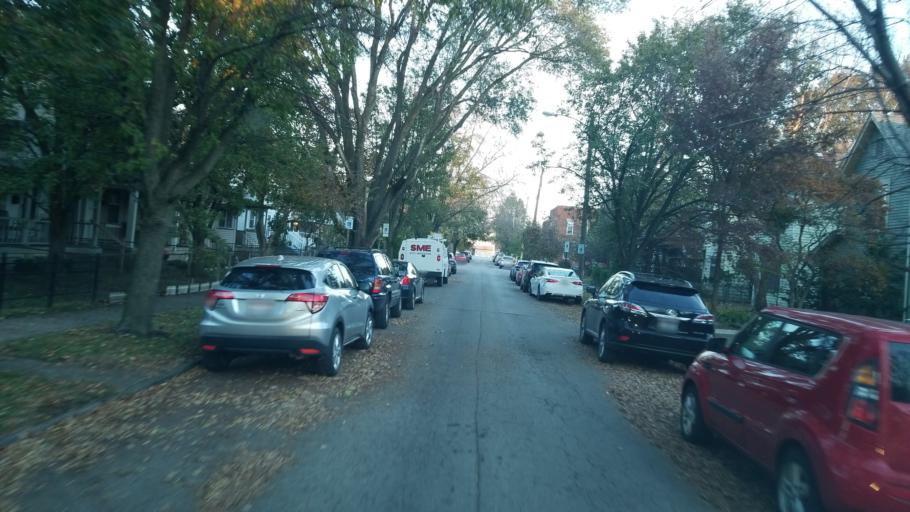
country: US
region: Ohio
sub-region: Franklin County
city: Columbus
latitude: 39.9383
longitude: -82.9861
